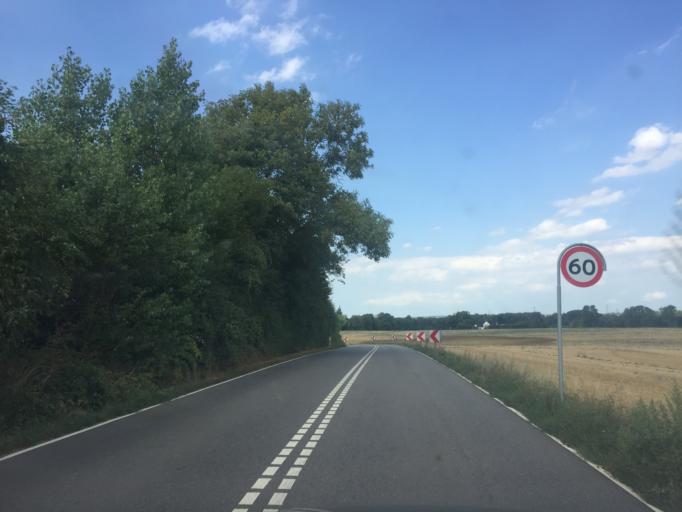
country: DK
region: Capital Region
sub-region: Egedal Kommune
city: Vekso
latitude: 55.7235
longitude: 12.2062
